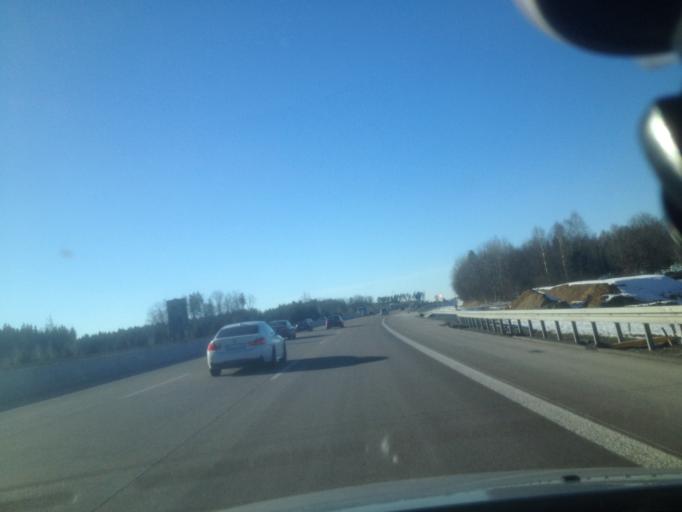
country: DE
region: Bavaria
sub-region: Swabia
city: Landensberg
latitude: 48.4003
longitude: 10.5411
